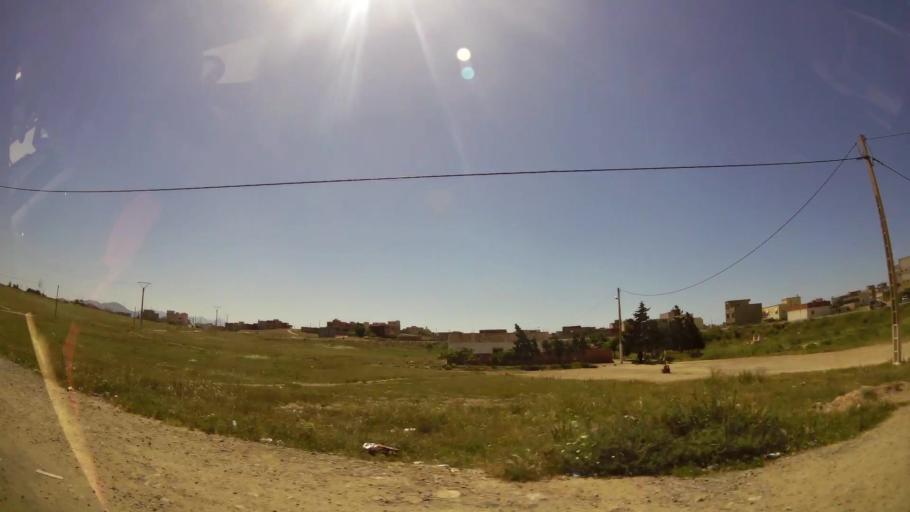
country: MA
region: Oriental
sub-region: Berkane-Taourirt
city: Madagh
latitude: 35.1316
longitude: -2.4246
